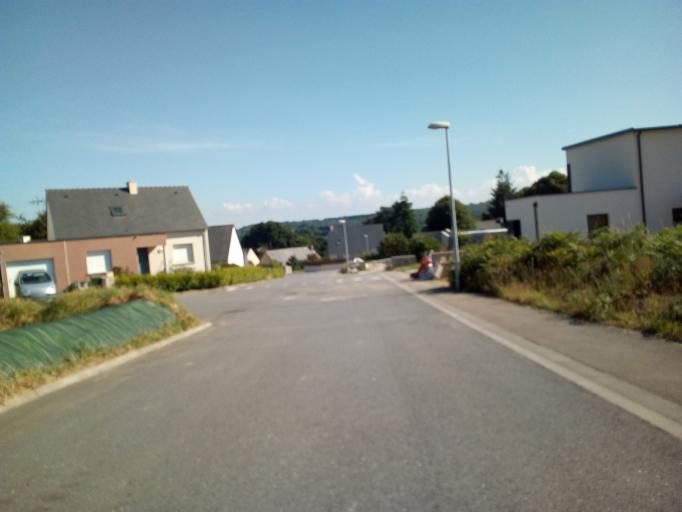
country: FR
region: Brittany
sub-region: Departement du Finistere
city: Landivisiau
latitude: 48.5083
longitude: -4.0877
